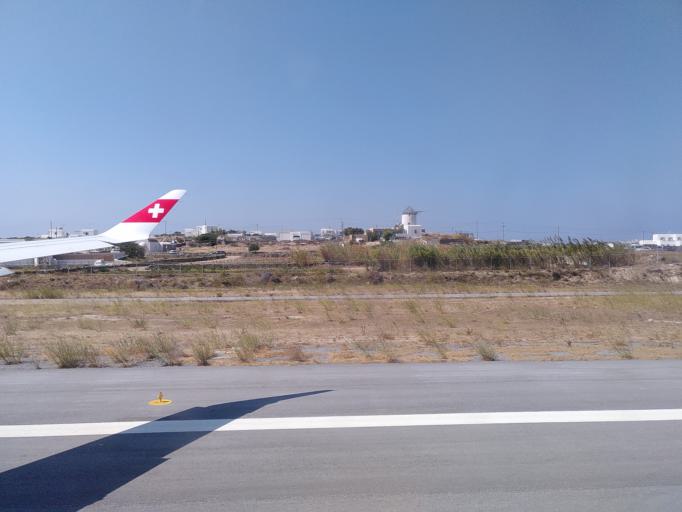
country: GR
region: South Aegean
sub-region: Nomos Kykladon
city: Mykonos
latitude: 37.4321
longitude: 25.3496
